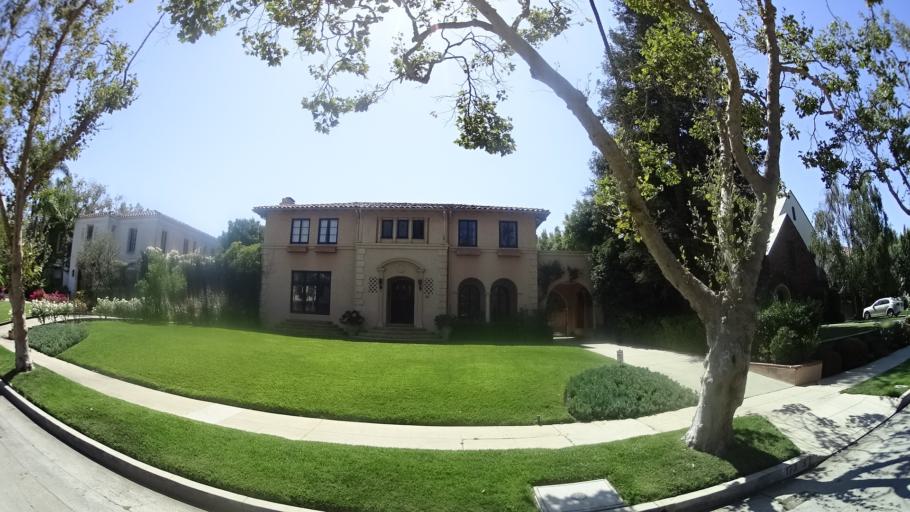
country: US
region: California
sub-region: Los Angeles County
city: Hollywood
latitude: 34.0715
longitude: -118.3359
